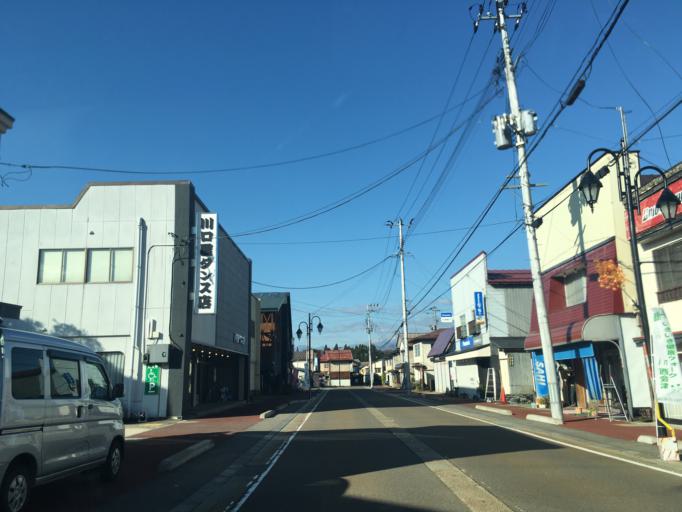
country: JP
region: Fukushima
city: Kitakata
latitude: 37.5879
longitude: 139.6449
